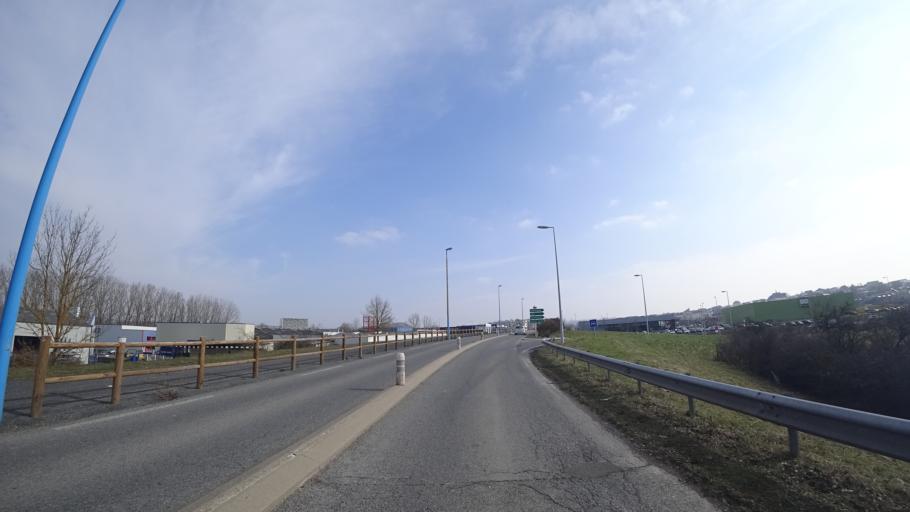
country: FR
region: Midi-Pyrenees
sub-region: Departement de l'Aveyron
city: Rodez
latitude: 44.3729
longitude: 2.5847
